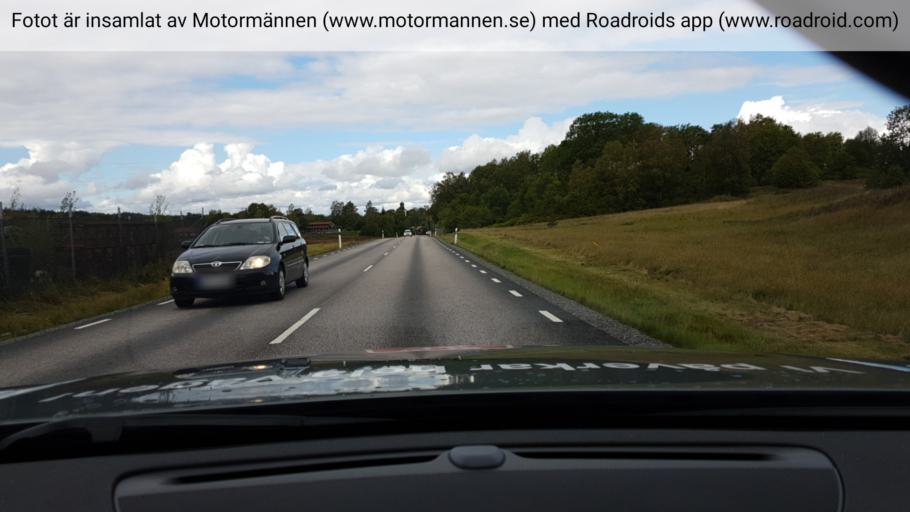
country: SE
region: Stockholm
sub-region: Nykvarns Kommun
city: Nykvarn
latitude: 59.1930
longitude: 17.4537
